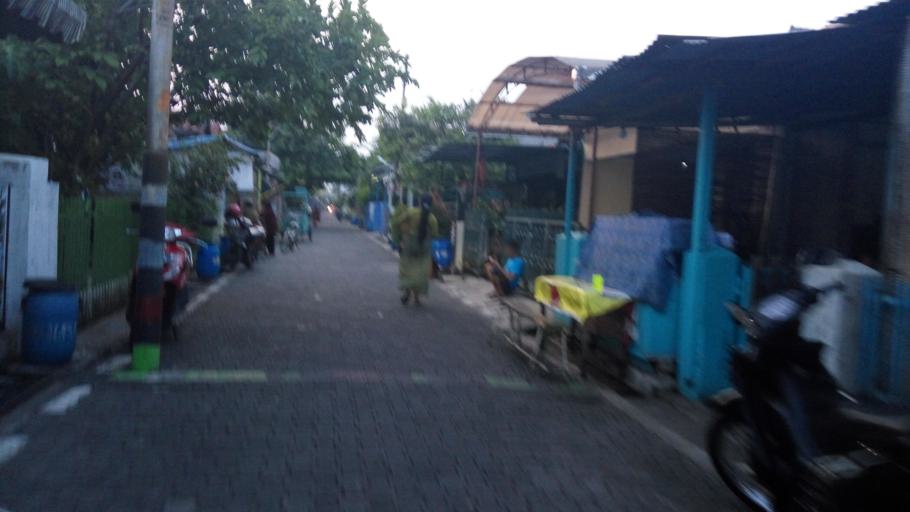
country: ID
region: Central Java
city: Semarang
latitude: -6.9843
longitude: 110.4051
